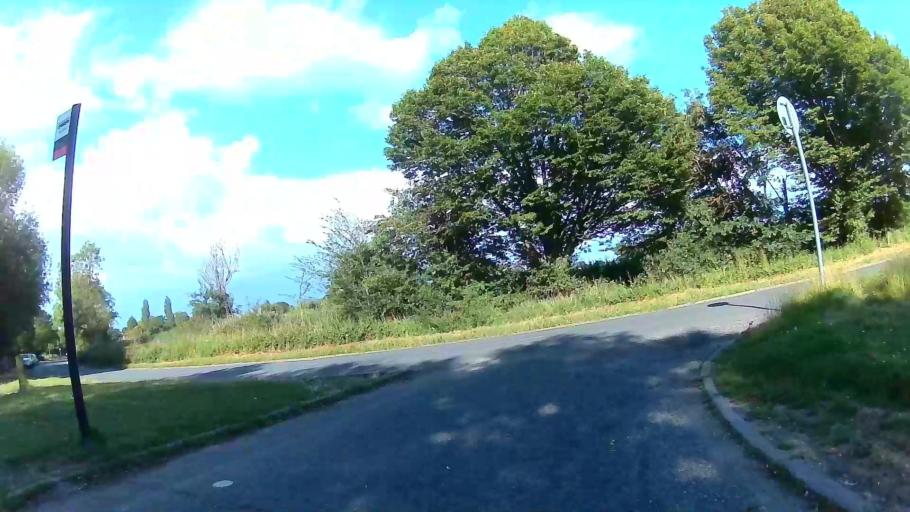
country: GB
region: England
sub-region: Essex
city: Kelvedon Hatch
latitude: 51.6919
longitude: 0.3212
